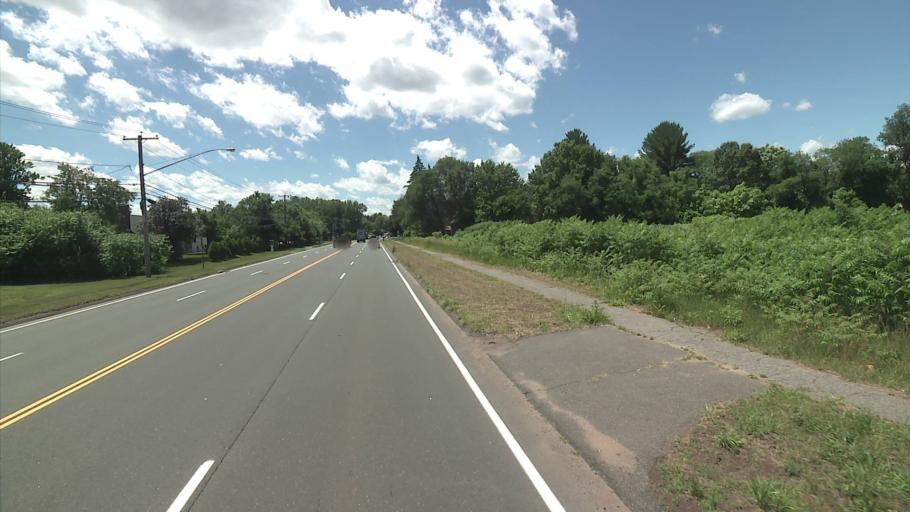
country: US
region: Connecticut
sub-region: Hartford County
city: Sherwood Manor
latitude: 42.0022
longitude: -72.5639
